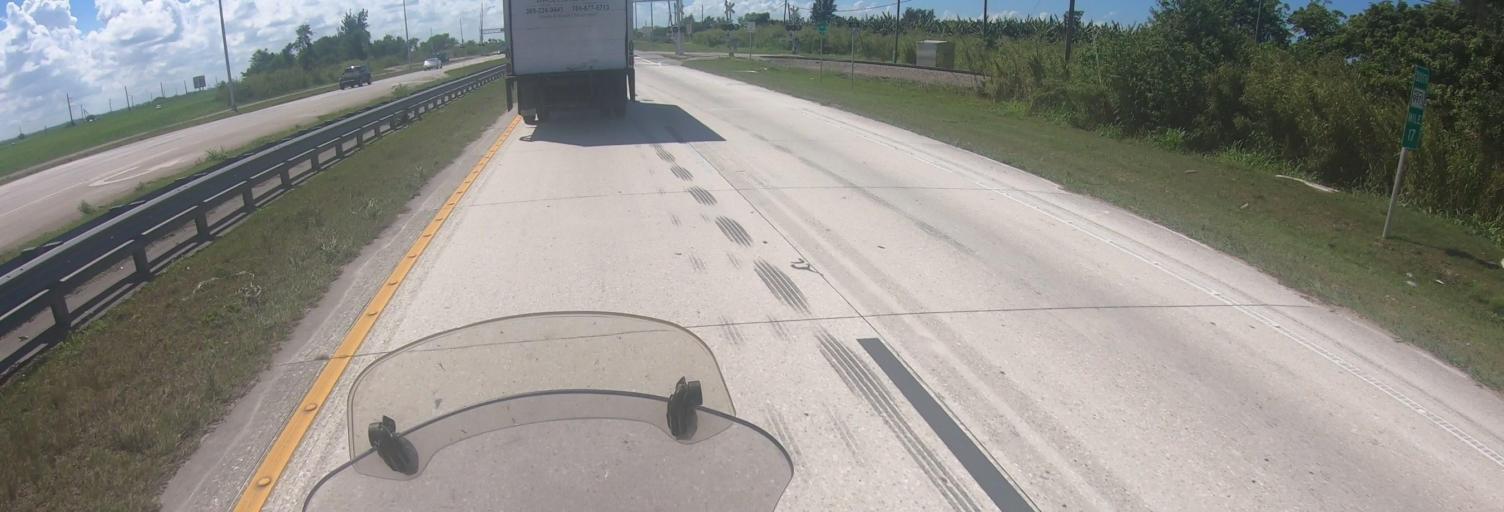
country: US
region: Florida
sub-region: Miami-Dade County
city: The Hammocks
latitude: 25.6833
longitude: -80.4792
